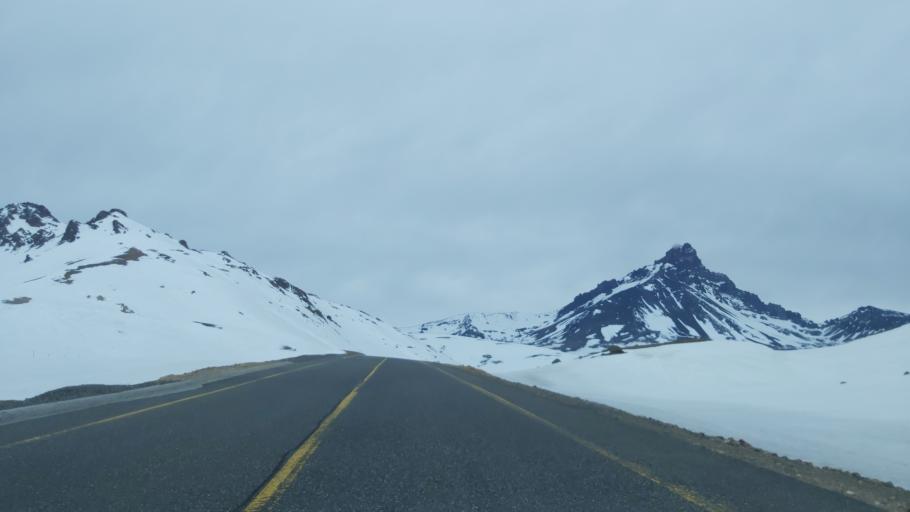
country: AR
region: Mendoza
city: Malargue
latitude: -35.9858
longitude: -70.3943
